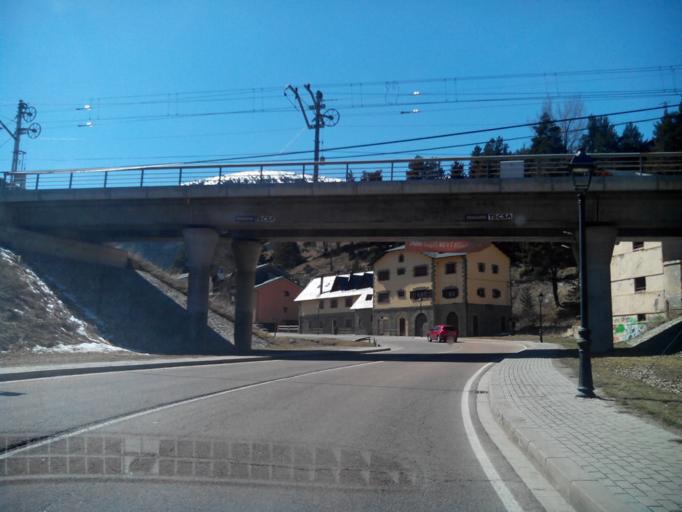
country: ES
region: Catalonia
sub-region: Provincia de Girona
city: Toses
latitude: 42.3434
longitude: 1.9573
